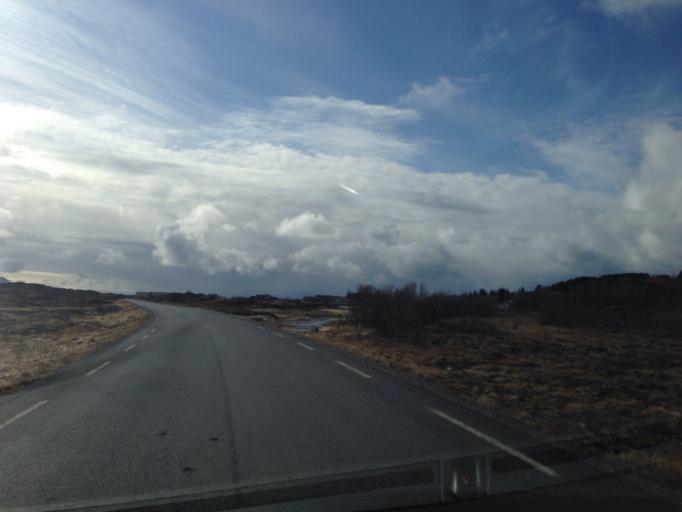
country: NO
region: Nordland
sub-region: Vagan
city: Kabelvag
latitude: 68.3855
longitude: 14.4346
